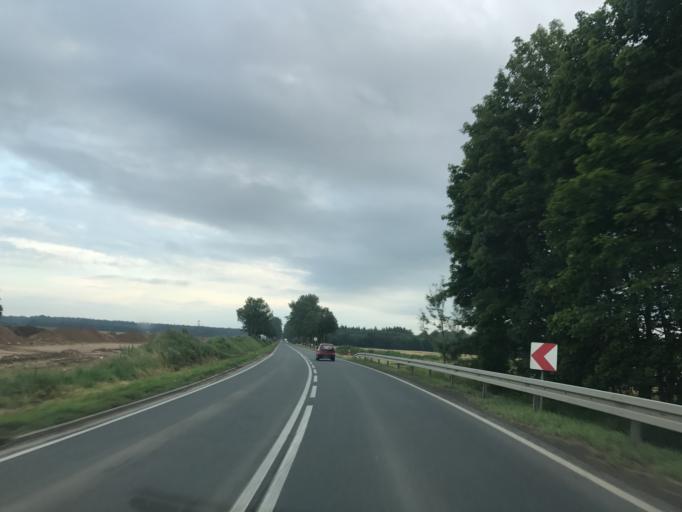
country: PL
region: West Pomeranian Voivodeship
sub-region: Powiat gryficki
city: Brojce
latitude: 53.8730
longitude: 15.3684
